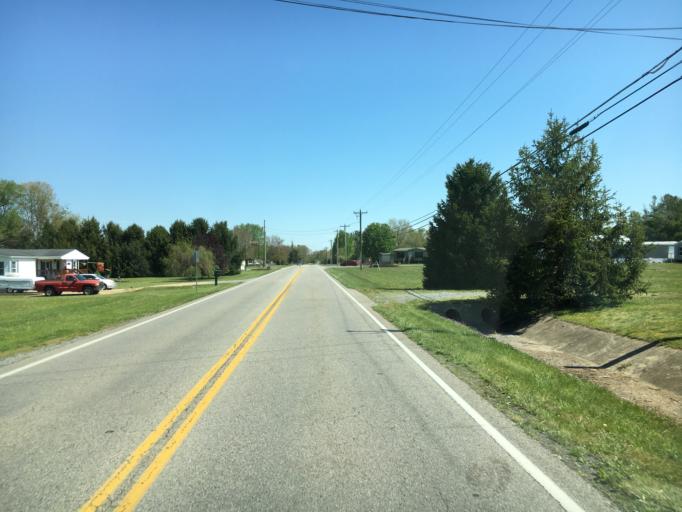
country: US
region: Virginia
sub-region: Augusta County
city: Crimora
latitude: 38.1752
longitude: -78.8470
